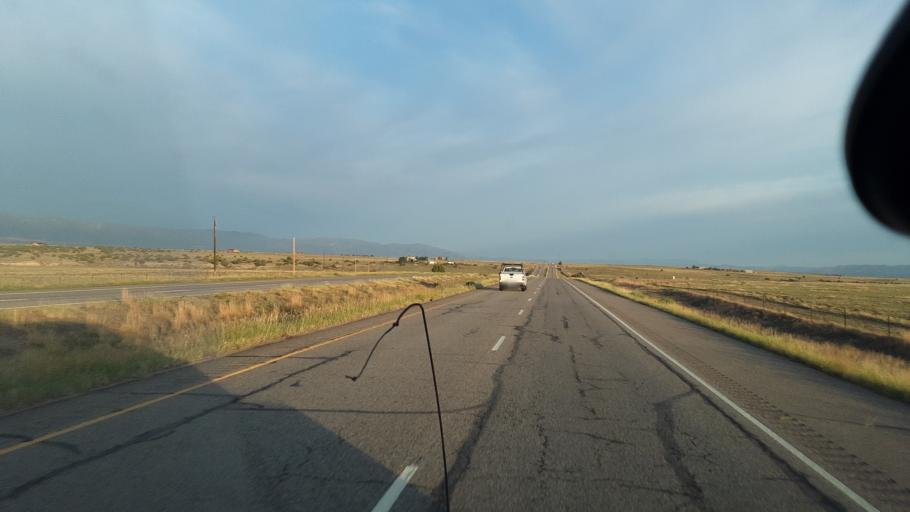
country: US
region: Colorado
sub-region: Pueblo County
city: Pueblo West
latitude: 38.3528
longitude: -104.8260
